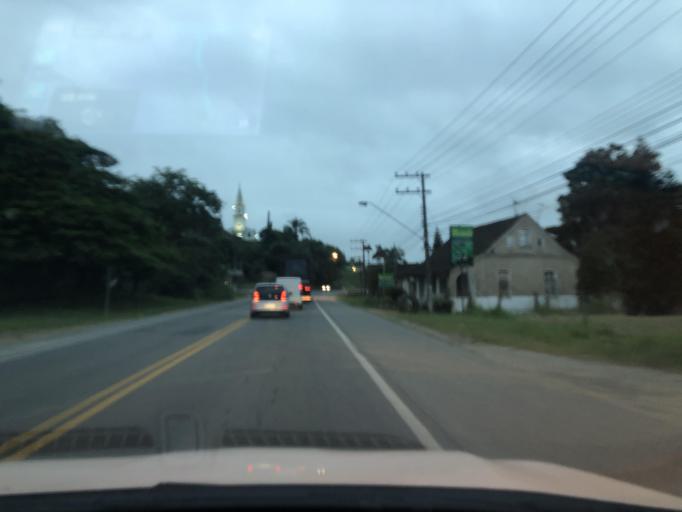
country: BR
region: Santa Catarina
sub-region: Pomerode
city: Pomerode
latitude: -26.7881
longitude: -49.0861
